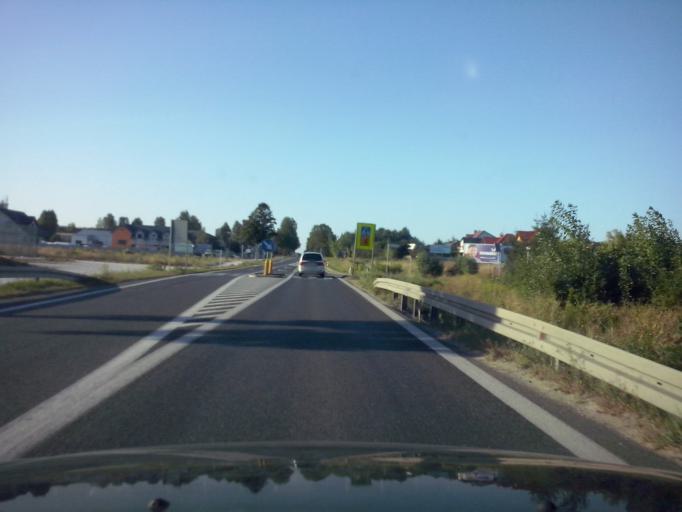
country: PL
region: Swietokrzyskie
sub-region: Powiat kielecki
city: Morawica
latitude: 50.7902
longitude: 20.6203
